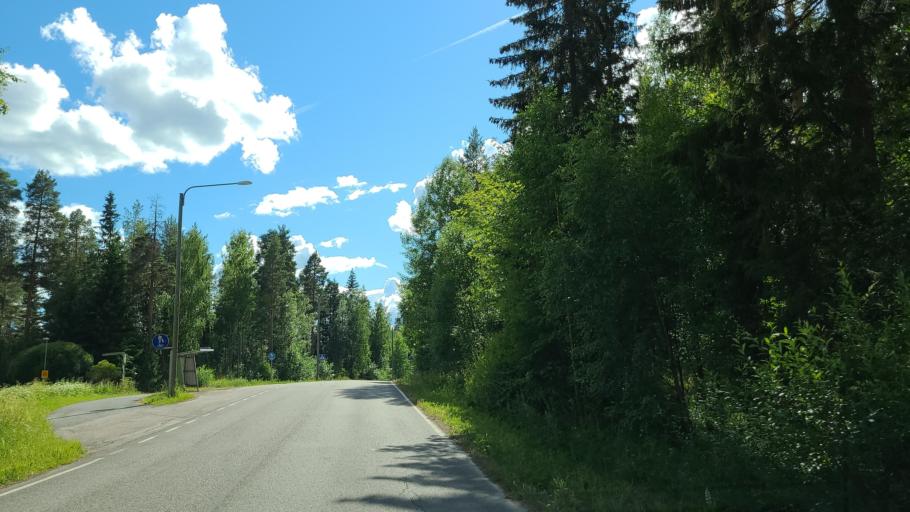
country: FI
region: Central Finland
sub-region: Jaemsae
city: Jaemsae
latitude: 61.8801
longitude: 25.2257
